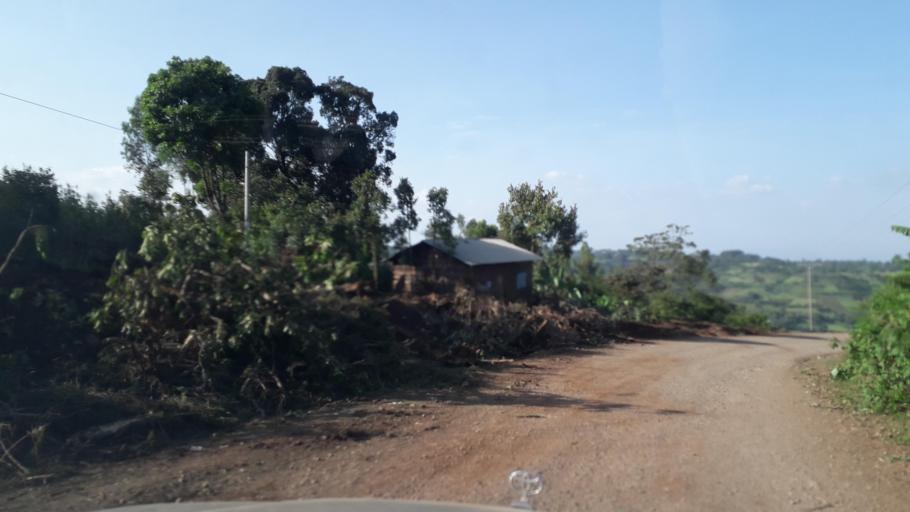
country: ET
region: Oromiya
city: Jima
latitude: 7.4704
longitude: 36.8765
